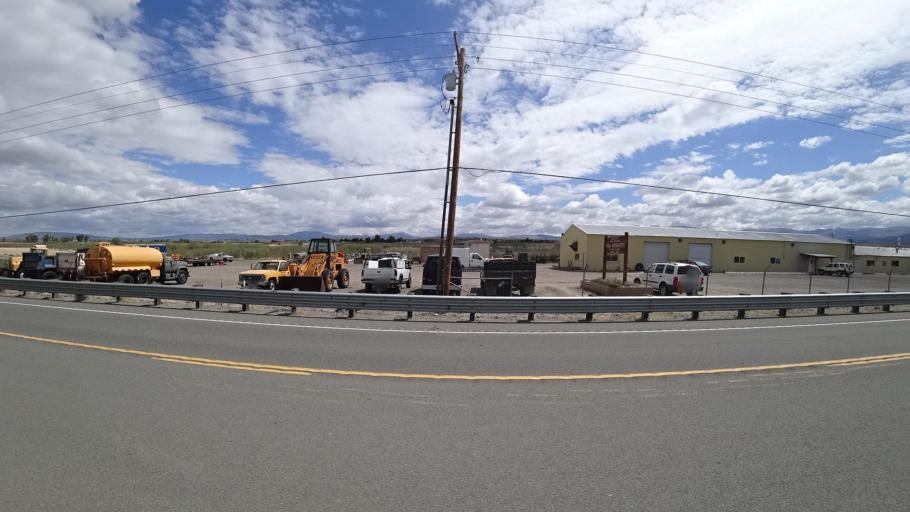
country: US
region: Nevada
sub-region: Douglas County
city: Gardnerville Ranchos
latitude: 38.9051
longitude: -119.7063
